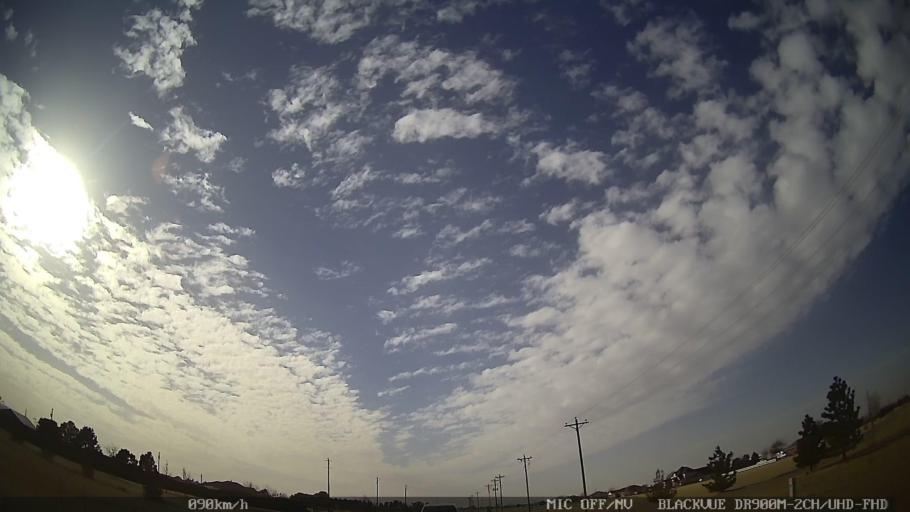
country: US
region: New Mexico
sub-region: Curry County
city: Texico
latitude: 34.4190
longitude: -103.1038
